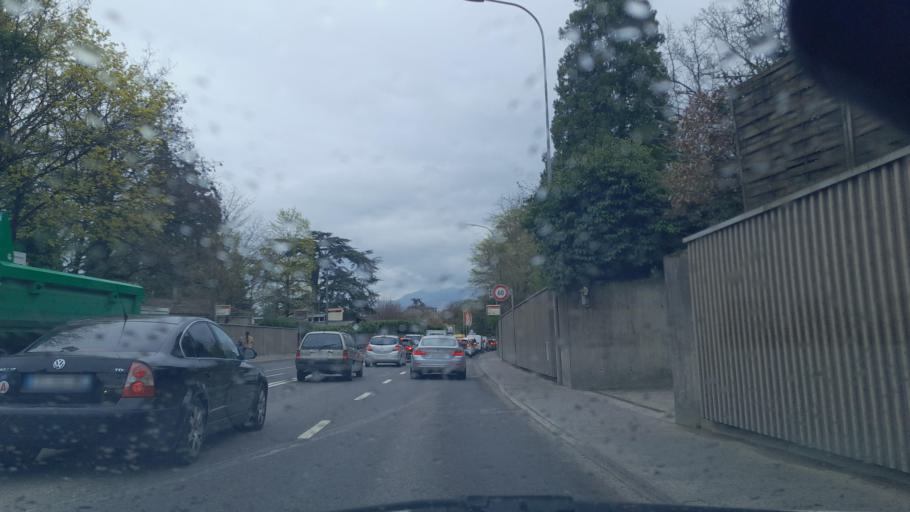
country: CH
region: Geneva
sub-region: Geneva
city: Vernier
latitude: 46.2198
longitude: 6.0881
